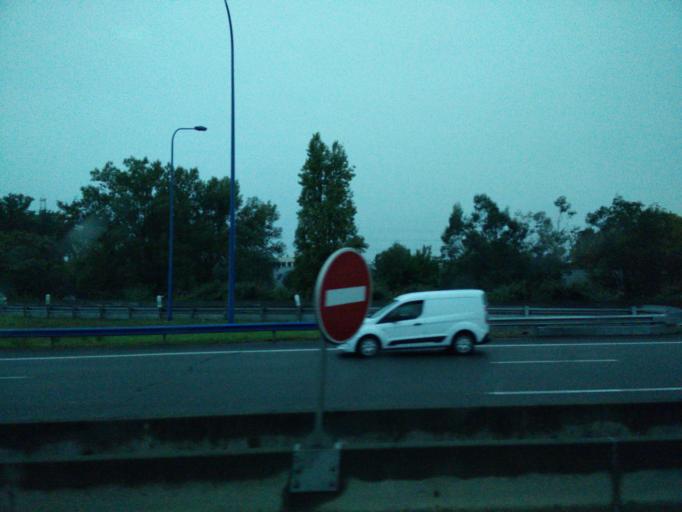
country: FR
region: Midi-Pyrenees
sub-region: Departement de la Haute-Garonne
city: Blagnac
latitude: 43.6256
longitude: 1.4189
